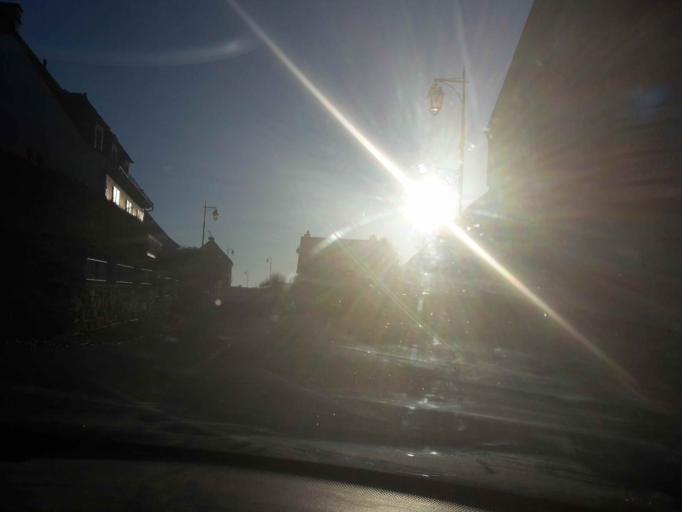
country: FR
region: Auvergne
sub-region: Departement du Cantal
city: Ydes
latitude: 45.2513
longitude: 2.5381
